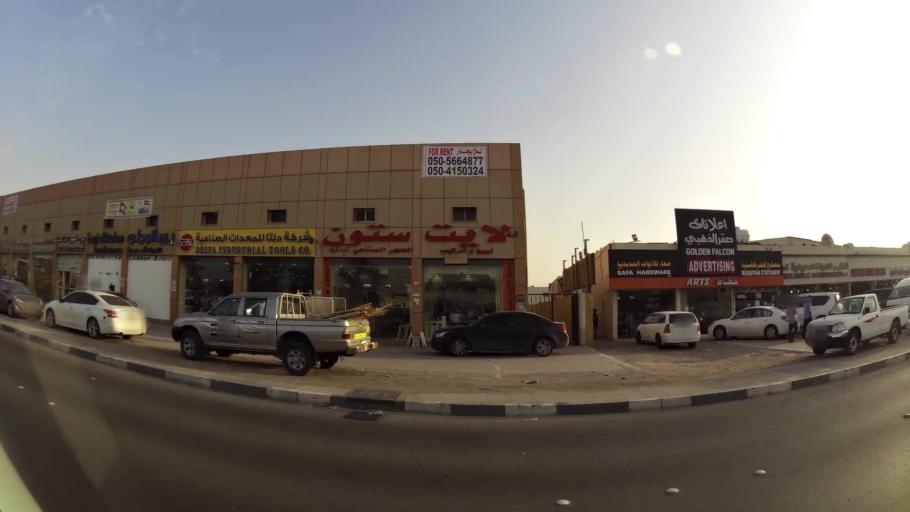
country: AE
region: Abu Dhabi
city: Abu Dhabi
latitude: 24.3728
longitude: 54.5046
